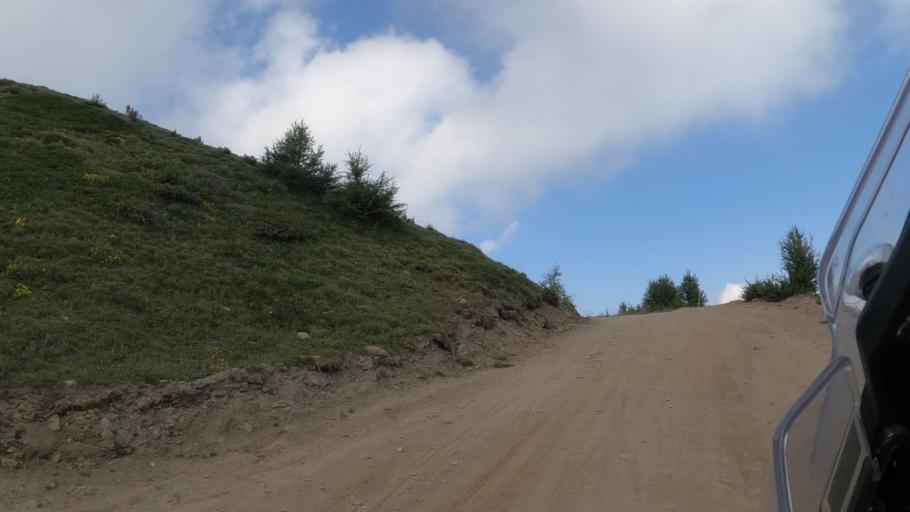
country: IT
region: Piedmont
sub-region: Provincia di Torino
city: Pragelato-Rua
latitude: 45.0352
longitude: 6.9095
